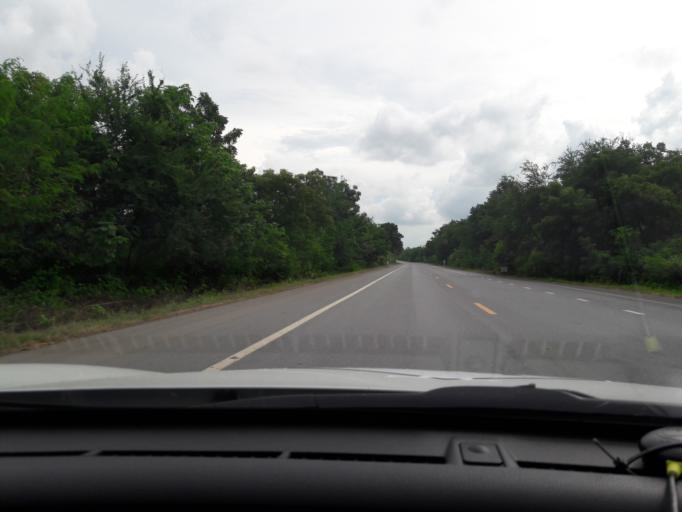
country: TH
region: Nakhon Sawan
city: Tak Fa
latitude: 15.3897
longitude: 100.5084
